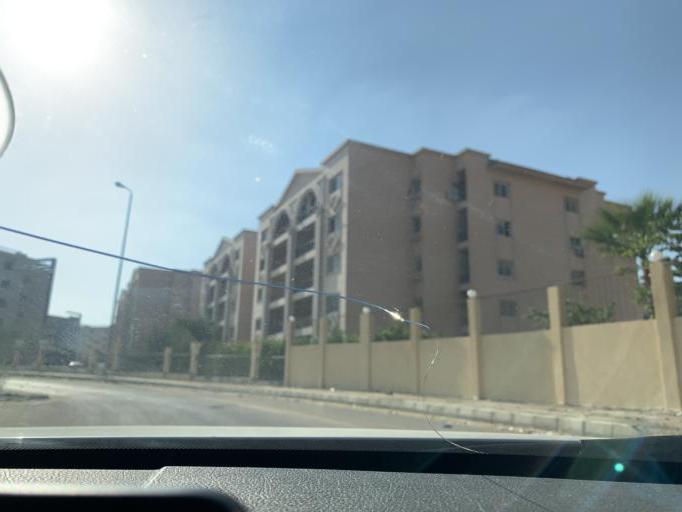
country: EG
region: Muhafazat al Qalyubiyah
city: Al Khankah
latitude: 30.0229
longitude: 31.4795
